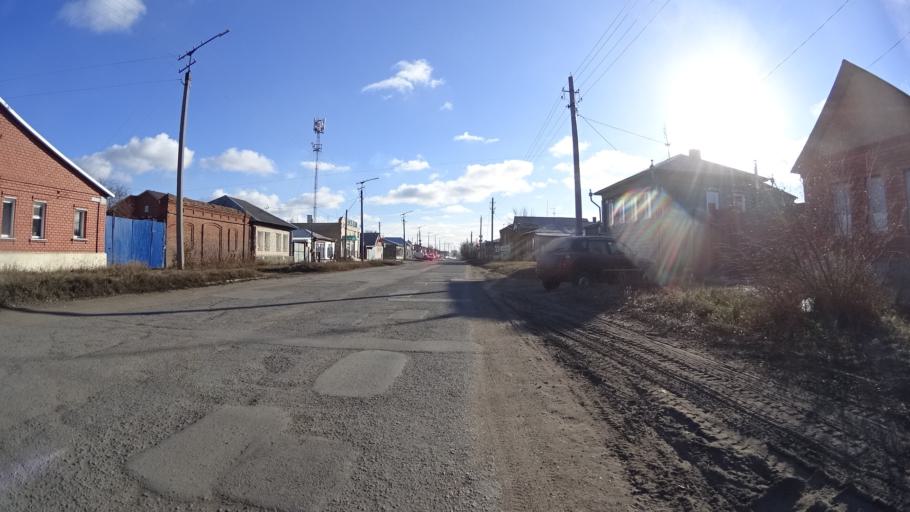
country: RU
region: Chelyabinsk
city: Troitsk
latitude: 54.0862
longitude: 61.5660
